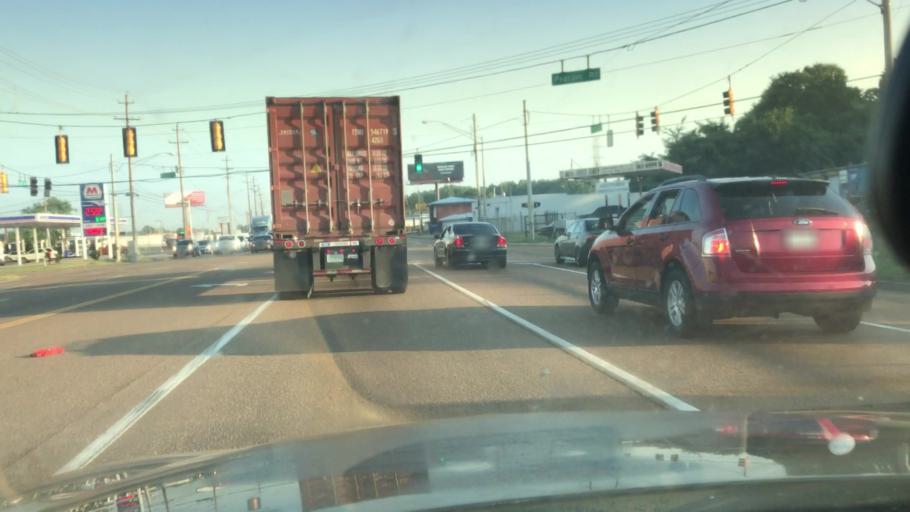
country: US
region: Mississippi
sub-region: De Soto County
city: Southaven
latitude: 35.0728
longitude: -89.9474
